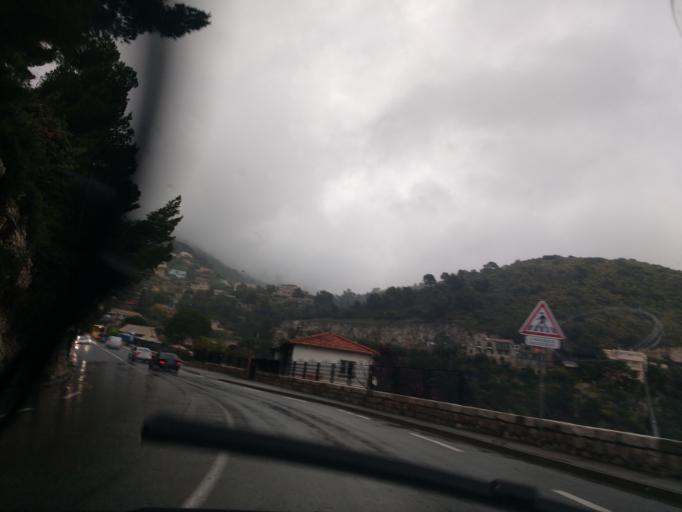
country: FR
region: Provence-Alpes-Cote d'Azur
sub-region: Departement des Alpes-Maritimes
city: Eze
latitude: 43.7222
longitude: 7.3798
